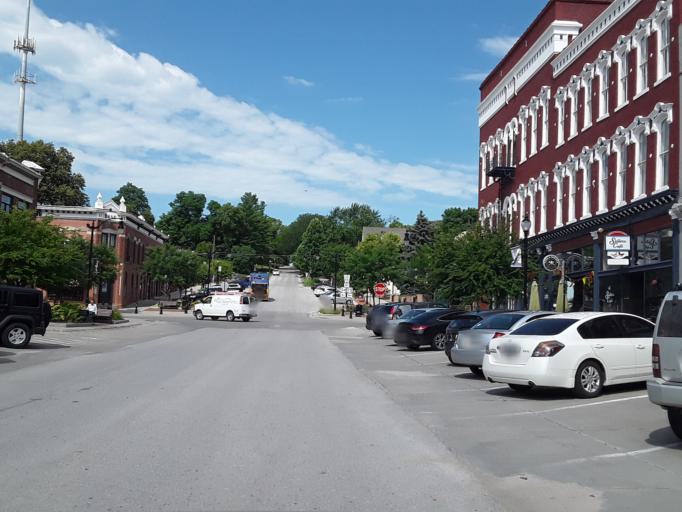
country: US
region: Nebraska
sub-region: Cass County
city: Plattsmouth
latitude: 41.0112
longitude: -95.8854
